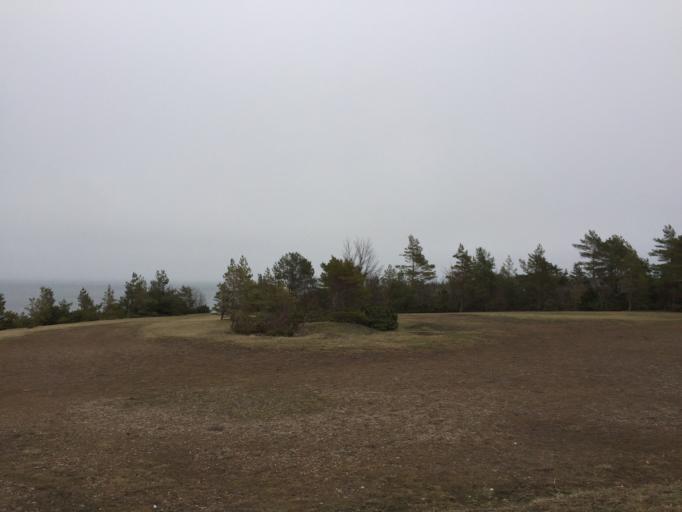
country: EE
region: Saare
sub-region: Kuressaare linn
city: Kuressaare
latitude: 58.5702
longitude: 22.2882
